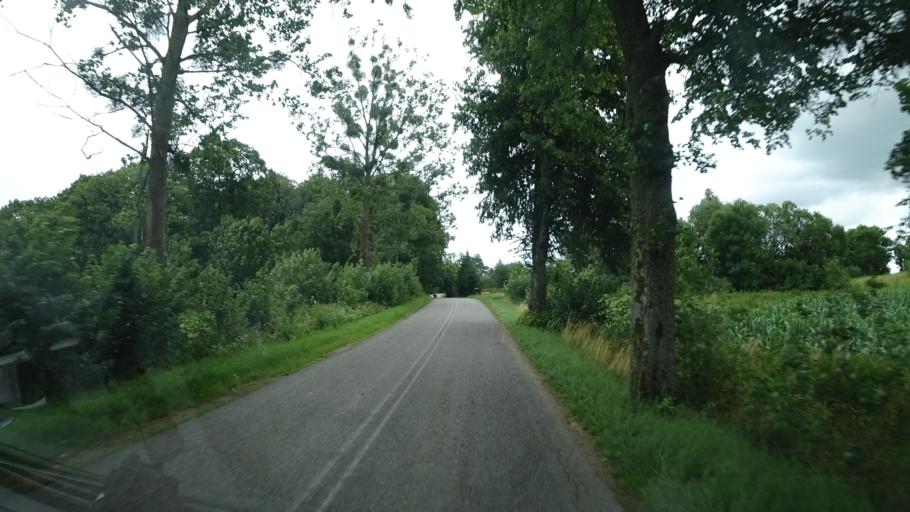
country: PL
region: Warmian-Masurian Voivodeship
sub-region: Powiat olecki
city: Kowale Oleckie
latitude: 54.2891
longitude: 22.5090
